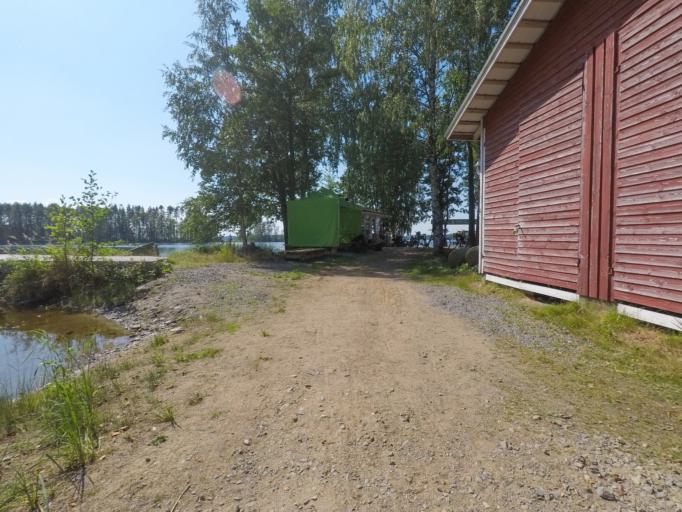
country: FI
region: Southern Savonia
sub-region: Mikkeli
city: Puumala
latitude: 61.4307
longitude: 28.0015
